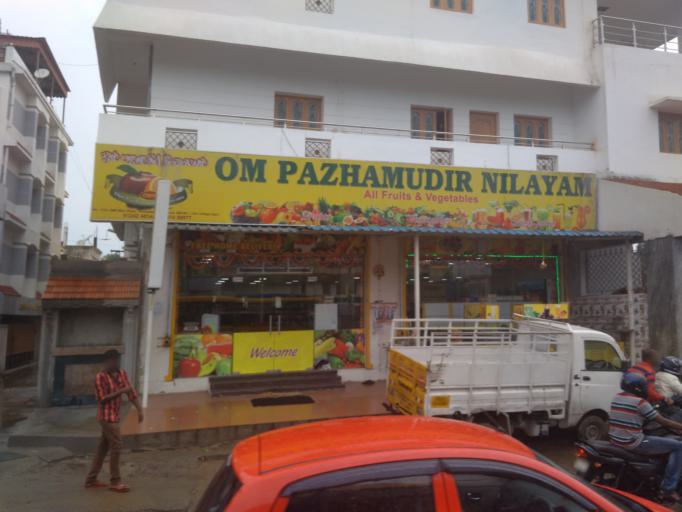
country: IN
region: Tamil Nadu
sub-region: Kancheepuram
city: Perungudi
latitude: 12.9457
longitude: 80.2392
